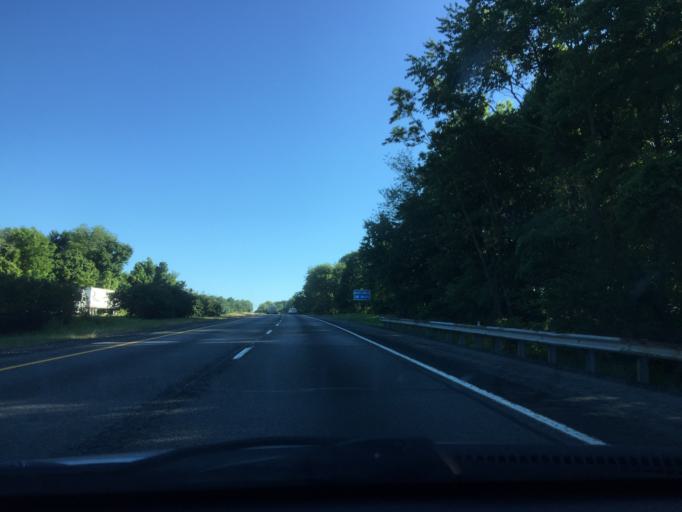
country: US
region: Maryland
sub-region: Baltimore County
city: Hunt Valley
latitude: 39.5174
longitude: -76.6617
